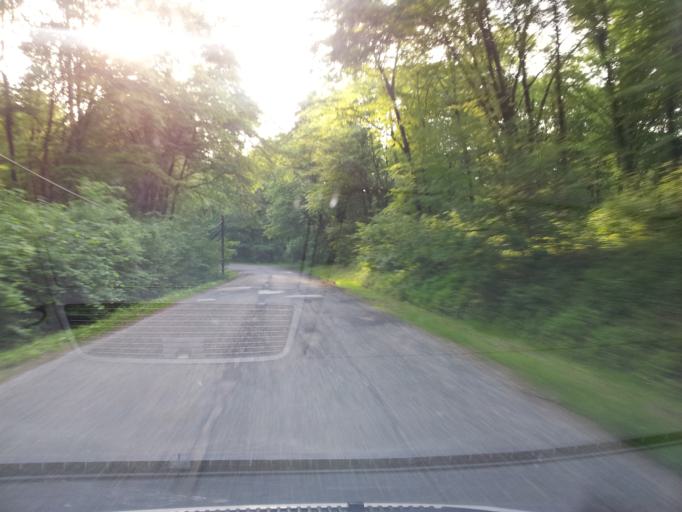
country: HU
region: Komarom-Esztergom
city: Kesztolc
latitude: 47.7321
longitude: 18.8309
